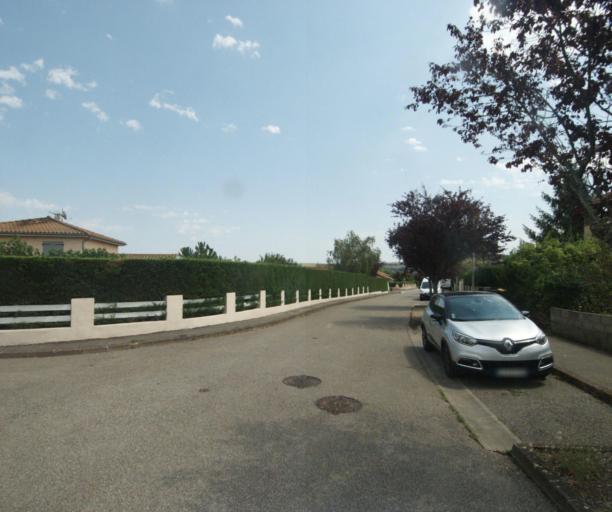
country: FR
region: Rhone-Alpes
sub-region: Departement du Rhone
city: Saint-Germain-Nuelles
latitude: 45.8441
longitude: 4.6063
